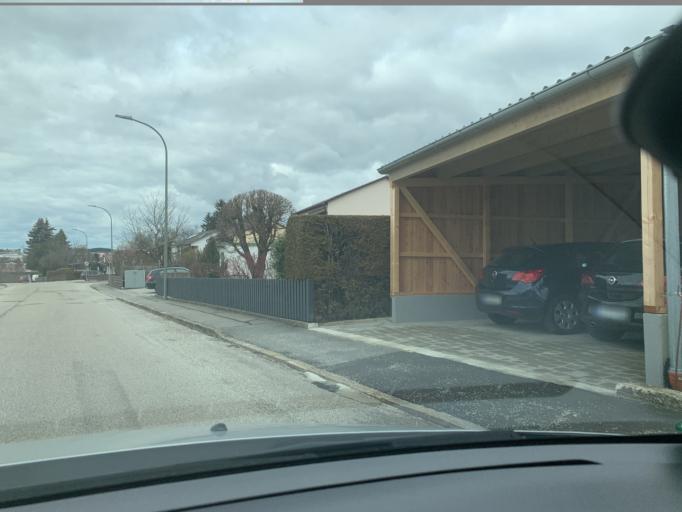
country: DE
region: Bavaria
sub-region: Lower Bavaria
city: Vilsbiburg
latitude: 48.4425
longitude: 12.3585
